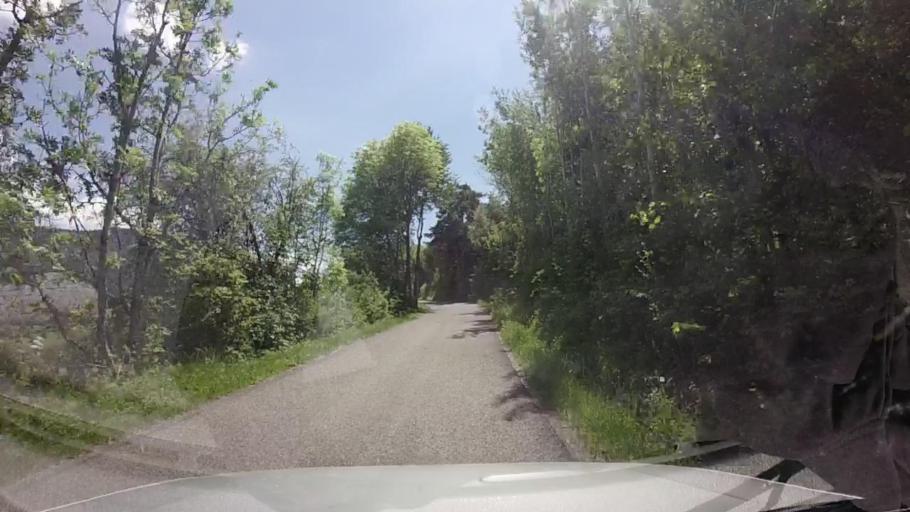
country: FR
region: Provence-Alpes-Cote d'Azur
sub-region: Departement des Alpes-de-Haute-Provence
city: Seyne-les-Alpes
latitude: 44.3342
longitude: 6.3452
